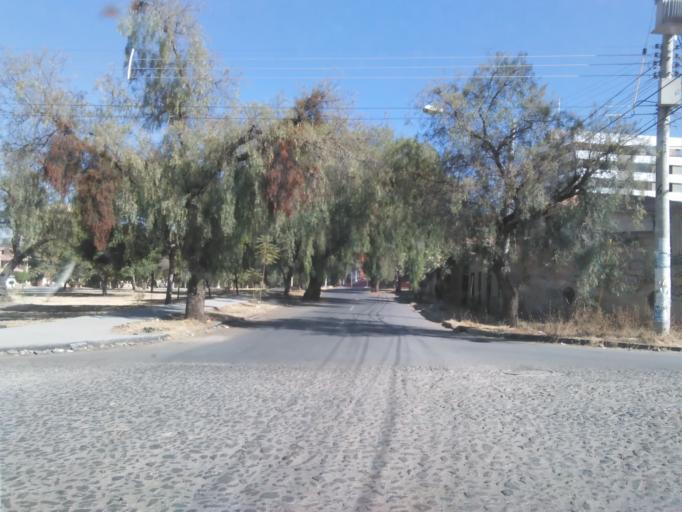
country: BO
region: Cochabamba
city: Cochabamba
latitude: -17.3712
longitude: -66.1446
